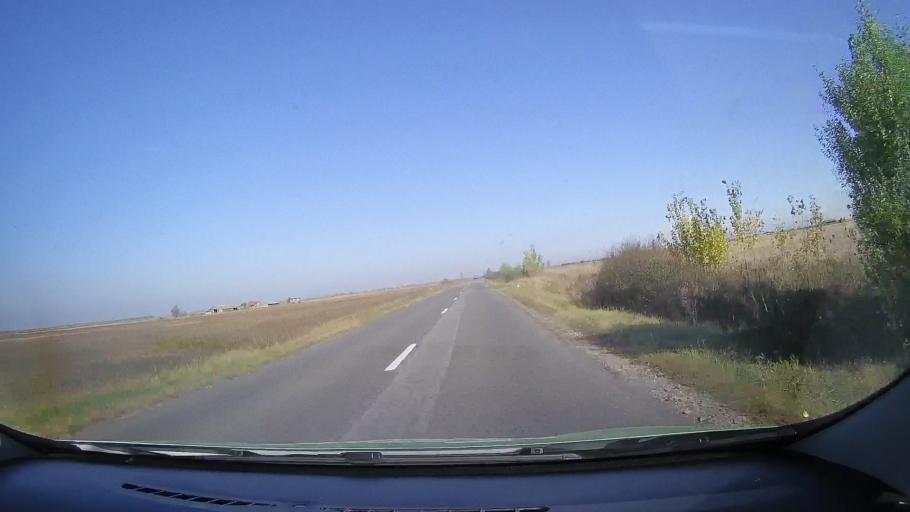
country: RO
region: Satu Mare
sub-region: Comuna Cauas
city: Cauas
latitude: 47.5313
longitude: 22.5665
